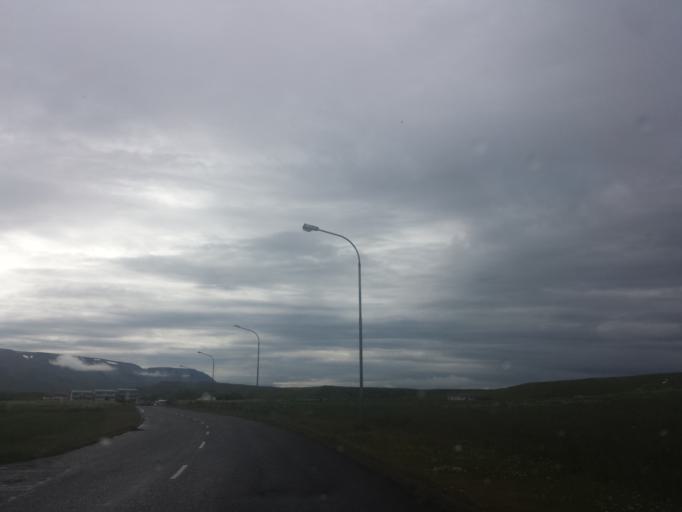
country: IS
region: Northwest
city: Saudarkrokur
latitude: 65.6591
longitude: -20.2987
